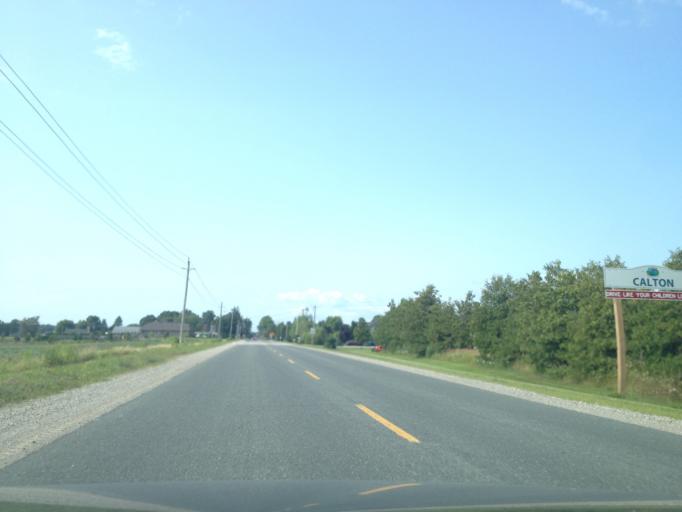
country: CA
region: Ontario
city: Aylmer
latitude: 42.7061
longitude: -80.8592
